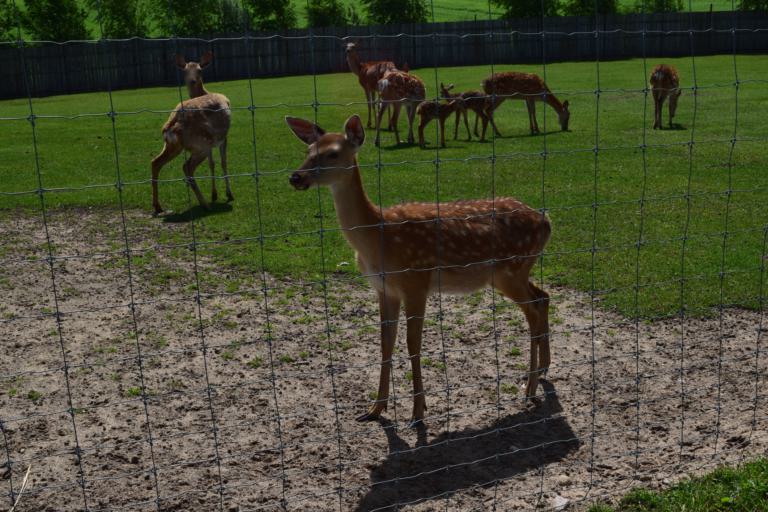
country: LT
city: Kalvarija
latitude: 54.3660
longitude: 23.1908
